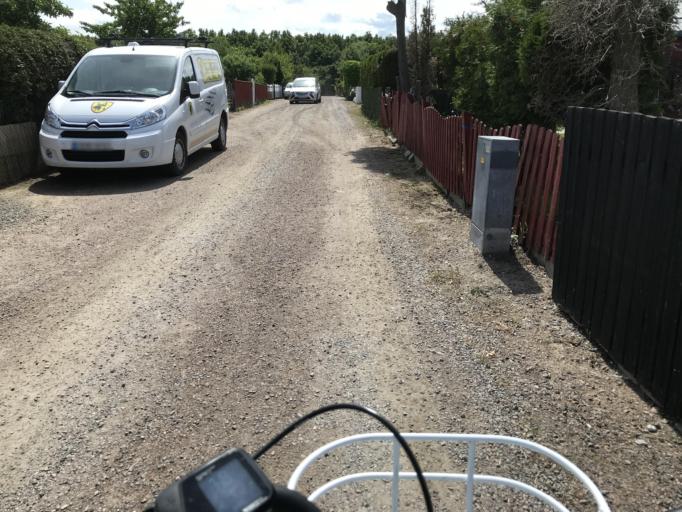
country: SE
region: Skane
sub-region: Landskrona
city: Landskrona
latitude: 55.8948
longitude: 12.8513
